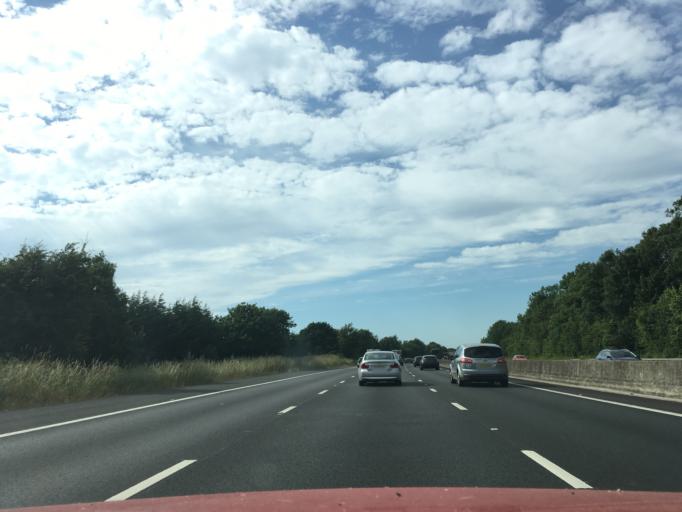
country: GB
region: England
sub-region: Wiltshire
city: Aldbourne
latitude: 51.4917
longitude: -1.5795
